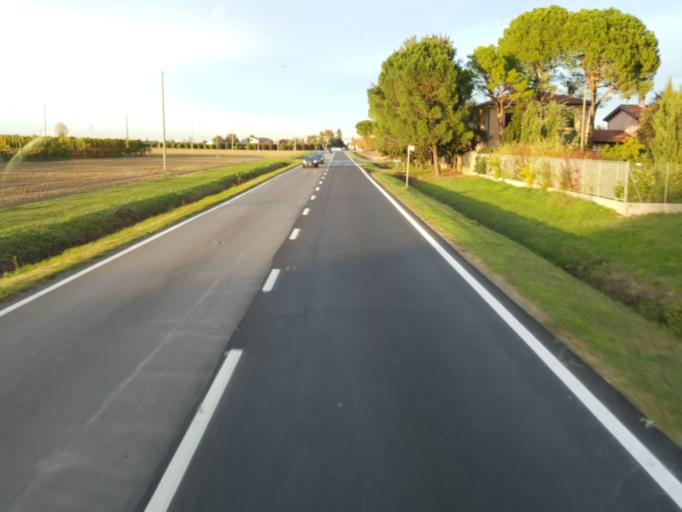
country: IT
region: Emilia-Romagna
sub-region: Provincia di Ravenna
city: Faenza
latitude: 44.3100
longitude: 11.8877
